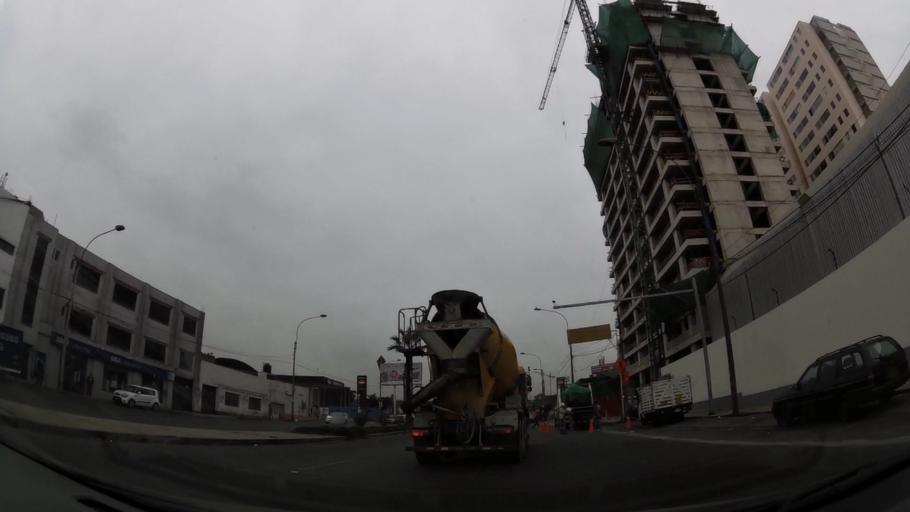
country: PE
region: Lima
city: Lima
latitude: -12.0561
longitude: -77.0588
